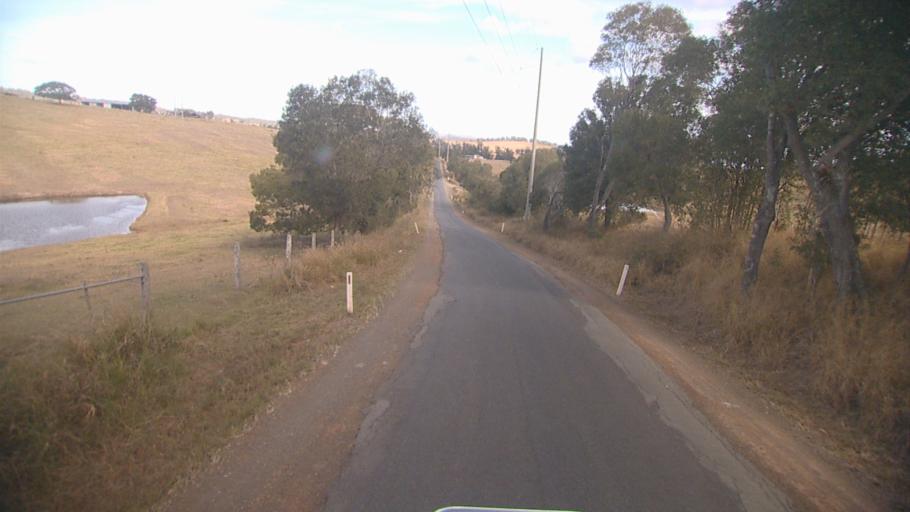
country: AU
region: Queensland
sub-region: Logan
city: Cedar Vale
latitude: -27.9064
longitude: 153.0137
